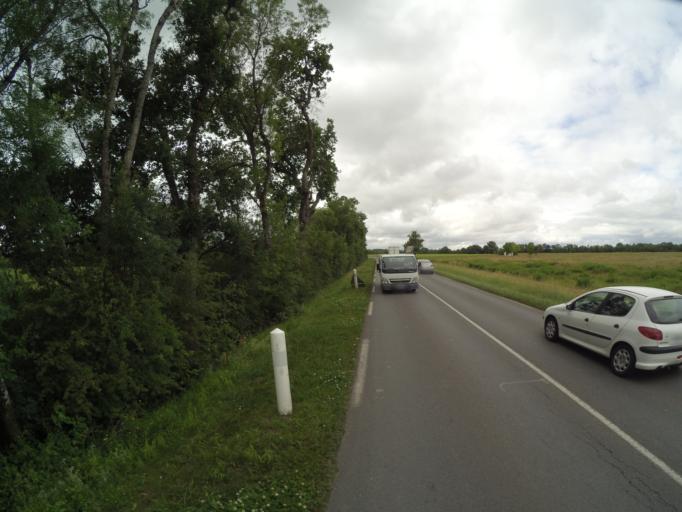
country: FR
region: Aquitaine
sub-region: Departement de la Gironde
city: Cantenac
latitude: 45.0263
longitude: -0.6462
